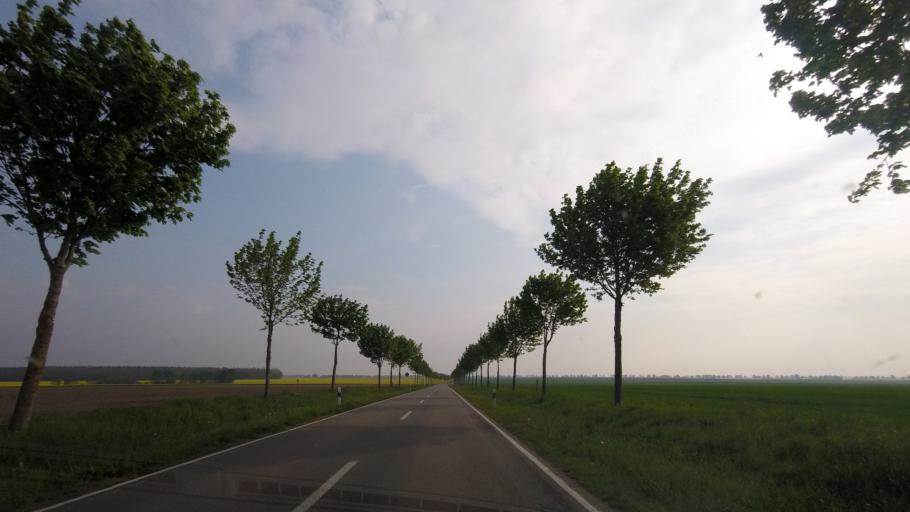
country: DE
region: Brandenburg
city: Juterbog
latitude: 51.9167
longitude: 13.0985
